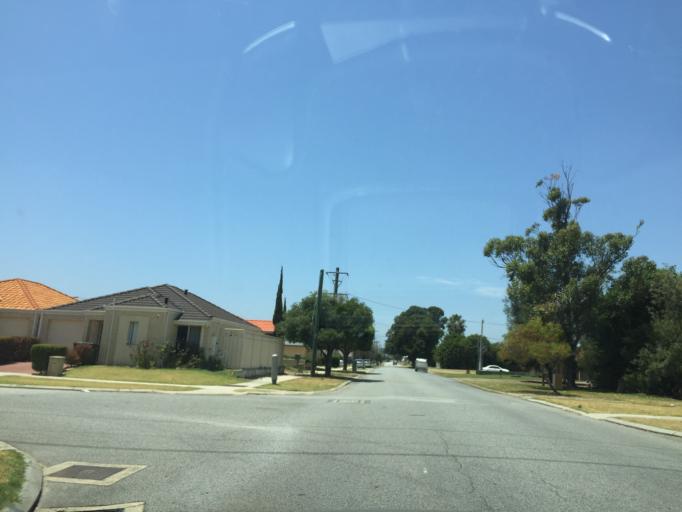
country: AU
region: Western Australia
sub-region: Canning
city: Queens Park
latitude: -32.0088
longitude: 115.9430
